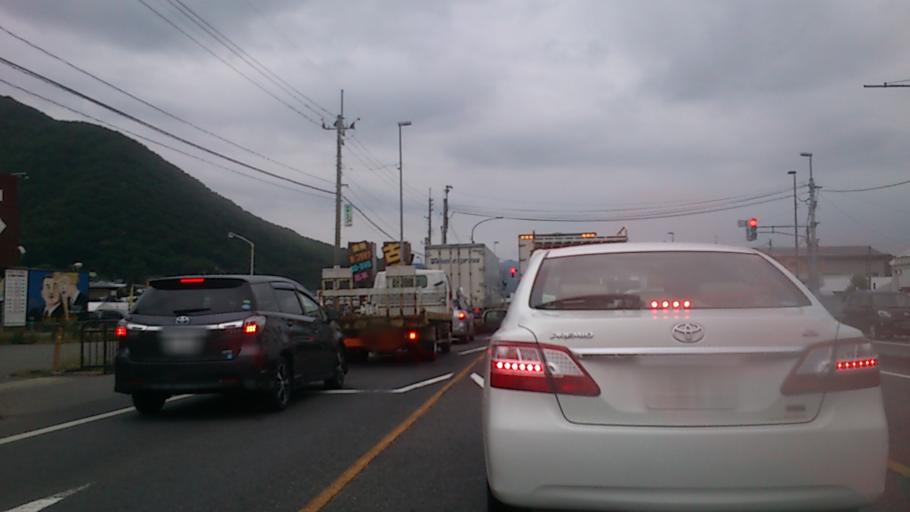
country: JP
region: Yamagata
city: Tendo
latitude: 38.3654
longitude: 140.3865
